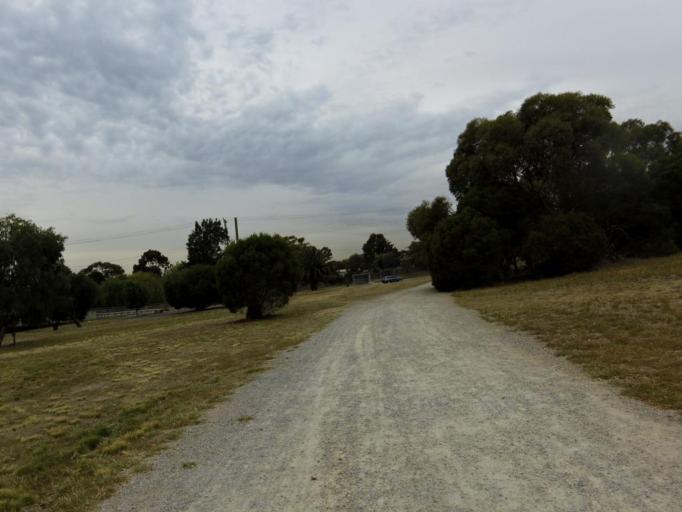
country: AU
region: Victoria
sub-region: Brimbank
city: Keilor Lodge
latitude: -37.7045
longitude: 144.8006
